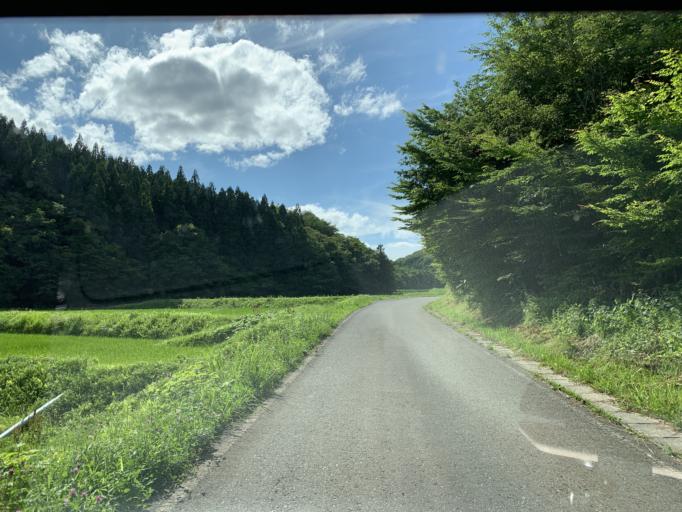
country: JP
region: Iwate
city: Ichinoseki
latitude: 38.9189
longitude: 140.9718
